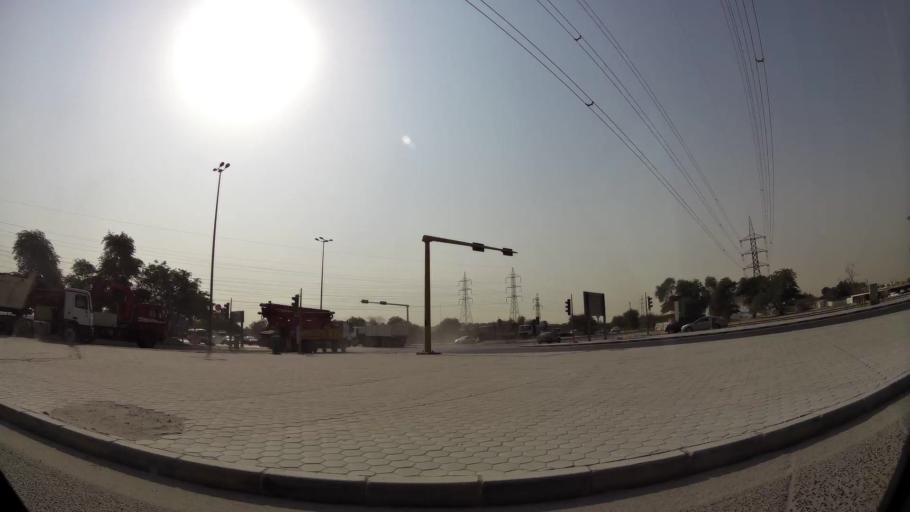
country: KW
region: Al Asimah
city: Ar Rabiyah
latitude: 29.2786
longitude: 47.8419
